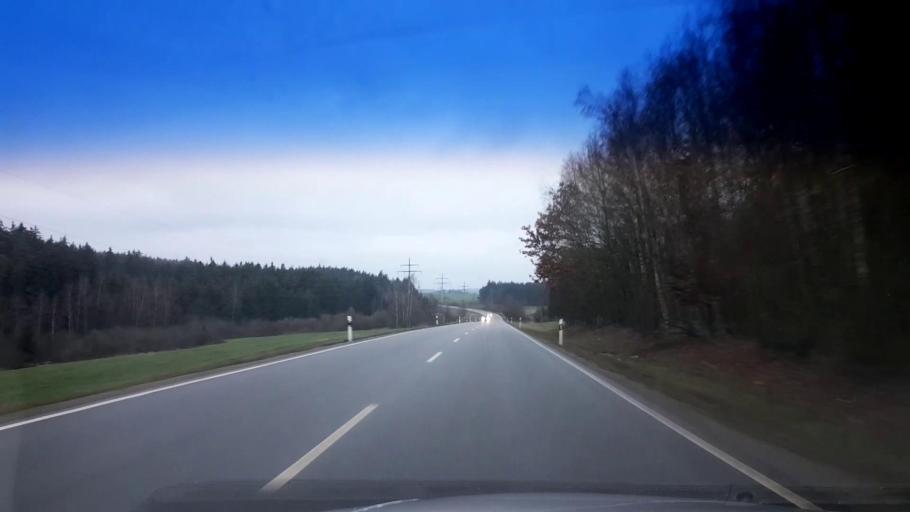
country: DE
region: Bavaria
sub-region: Upper Palatinate
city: Tirschenreuth
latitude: 49.8717
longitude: 12.2762
